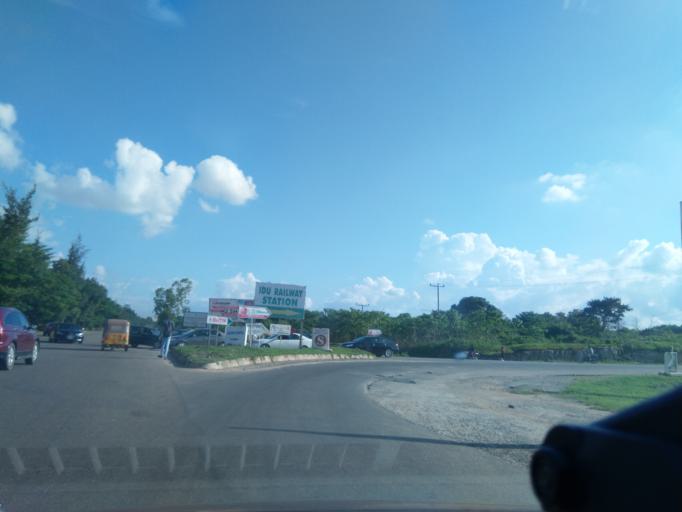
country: NG
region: Abuja Federal Capital Territory
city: Abuja
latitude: 9.0368
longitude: 7.4120
